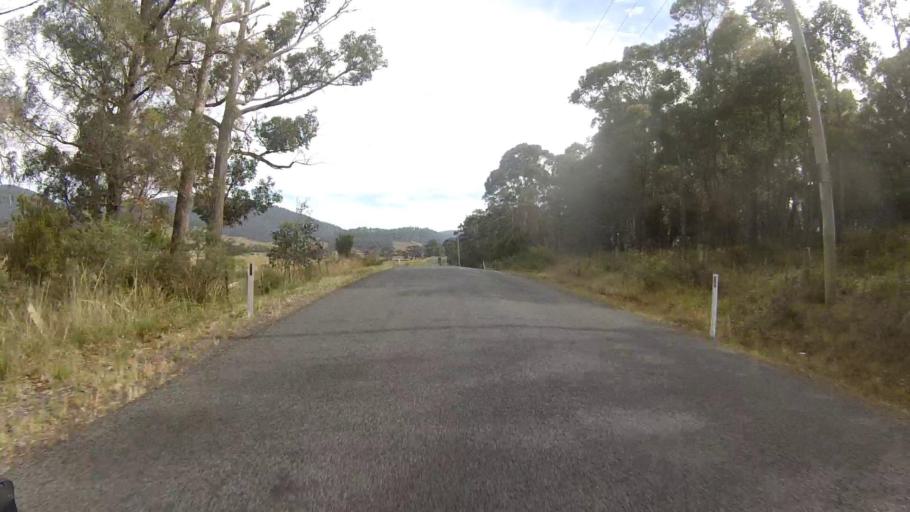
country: AU
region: Tasmania
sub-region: Sorell
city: Sorell
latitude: -42.8014
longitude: 147.7935
